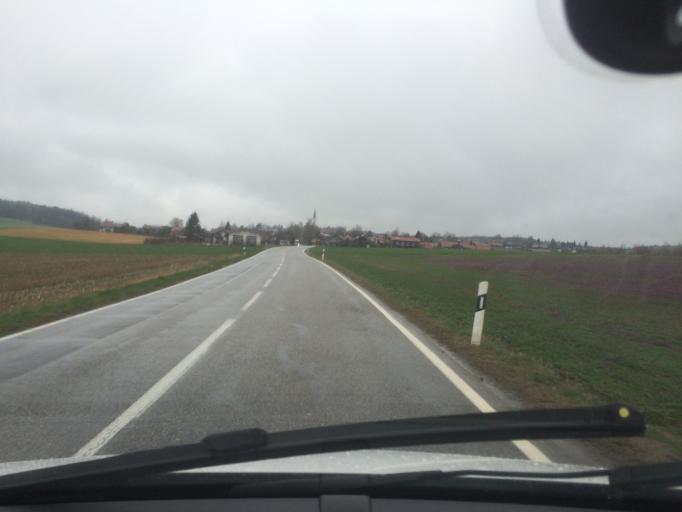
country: DE
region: Bavaria
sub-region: Upper Bavaria
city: Assling
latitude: 47.9705
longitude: 11.9603
